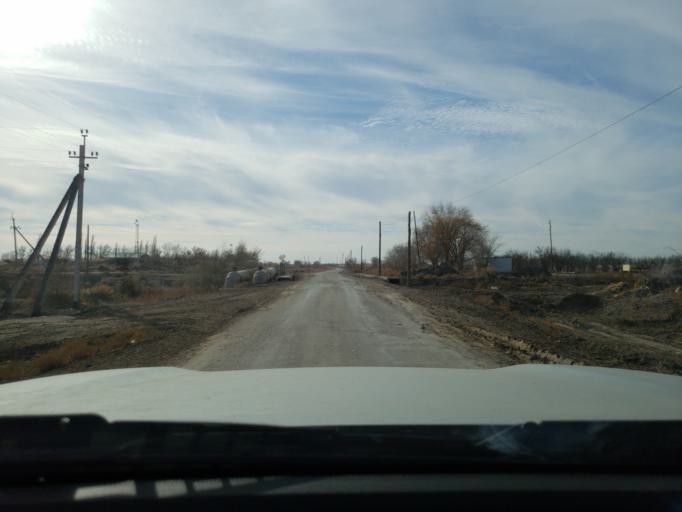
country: TM
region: Dasoguz
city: Dasoguz
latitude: 41.8454
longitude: 59.8756
